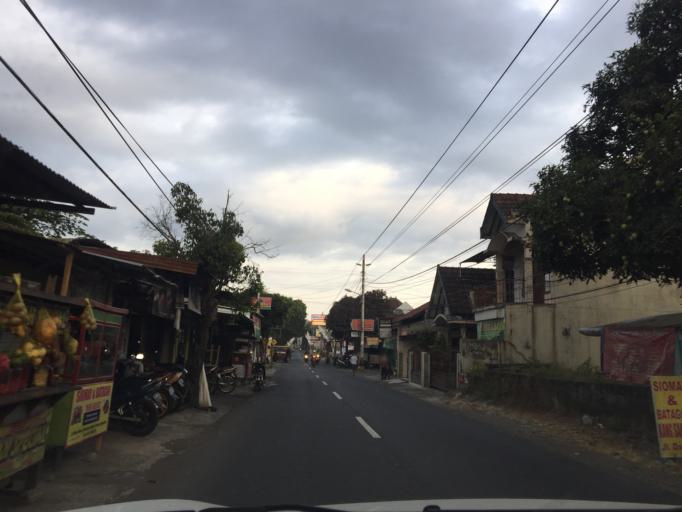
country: ID
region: Daerah Istimewa Yogyakarta
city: Melati
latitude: -7.7340
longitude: 110.3908
